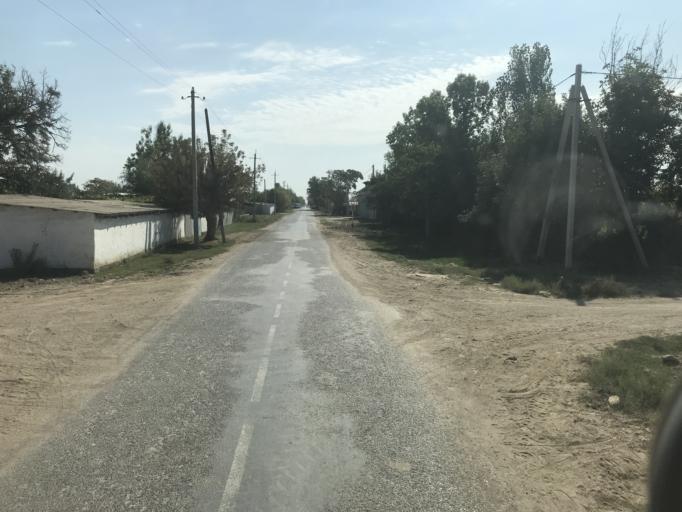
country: KZ
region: Ongtustik Qazaqstan
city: Myrzakent
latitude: 40.6643
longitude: 68.6155
